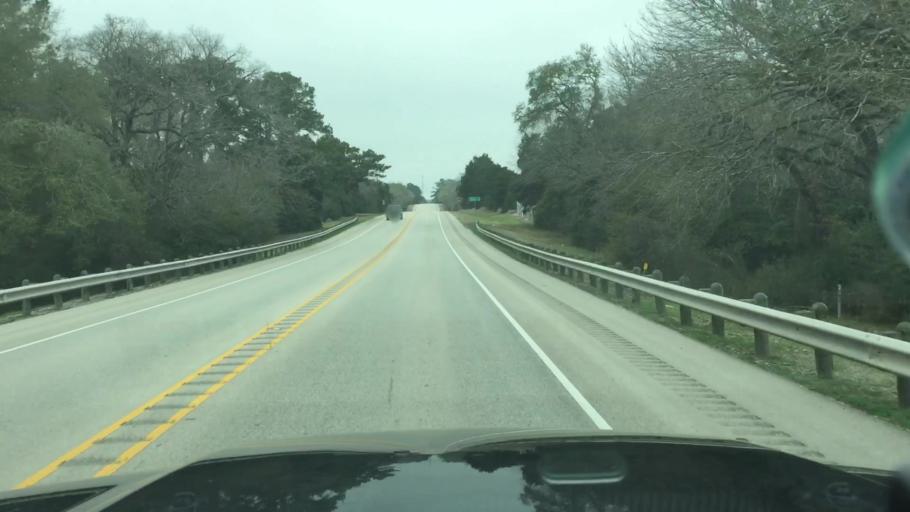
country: US
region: Texas
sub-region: Fayette County
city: La Grange
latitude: 30.0008
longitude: -96.8920
